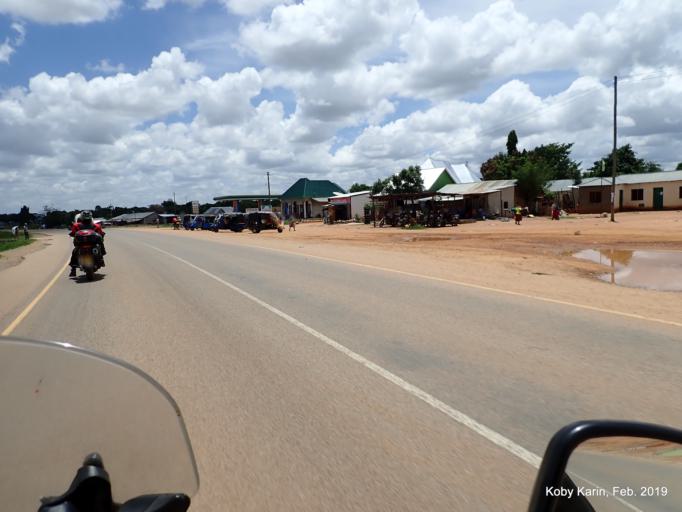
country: TZ
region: Shinyanga
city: Kahama
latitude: -3.8299
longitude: 32.5742
